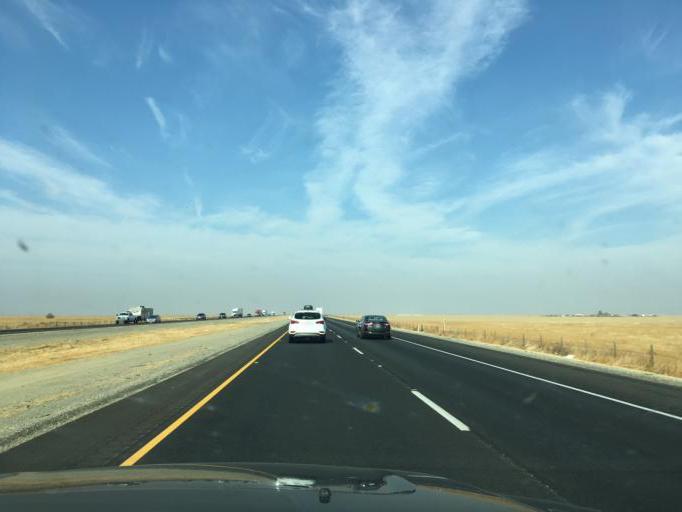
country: US
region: California
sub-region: Kern County
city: Lost Hills
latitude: 35.6720
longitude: -119.6945
